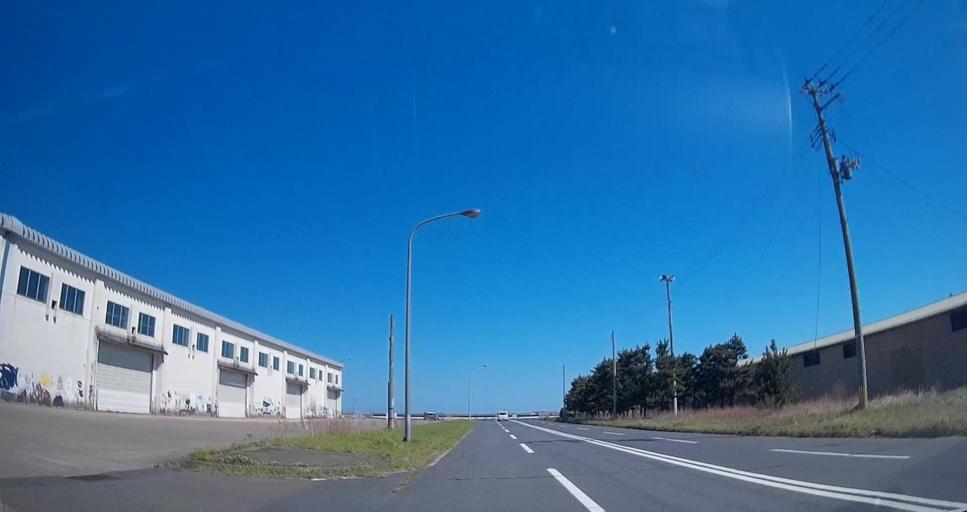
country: JP
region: Aomori
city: Hachinohe
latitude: 40.5298
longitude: 141.5444
